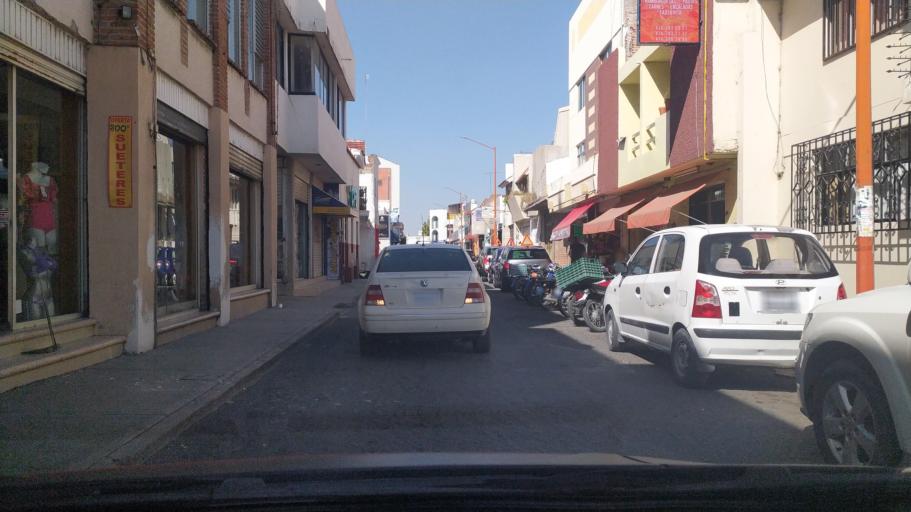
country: MX
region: Guanajuato
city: San Francisco del Rincon
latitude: 21.0185
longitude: -101.8557
